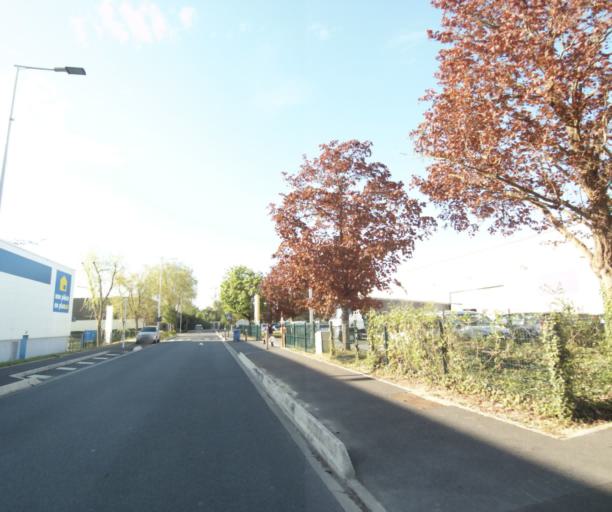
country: FR
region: Ile-de-France
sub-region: Departement de Seine-et-Marne
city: Torcy
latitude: 48.8446
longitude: 2.6601
